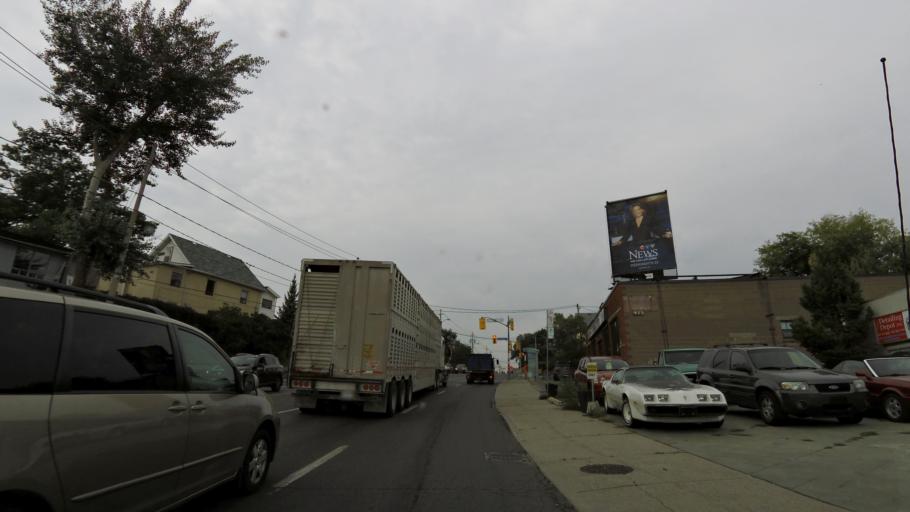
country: CA
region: Ontario
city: Toronto
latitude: 43.6840
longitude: -79.4833
